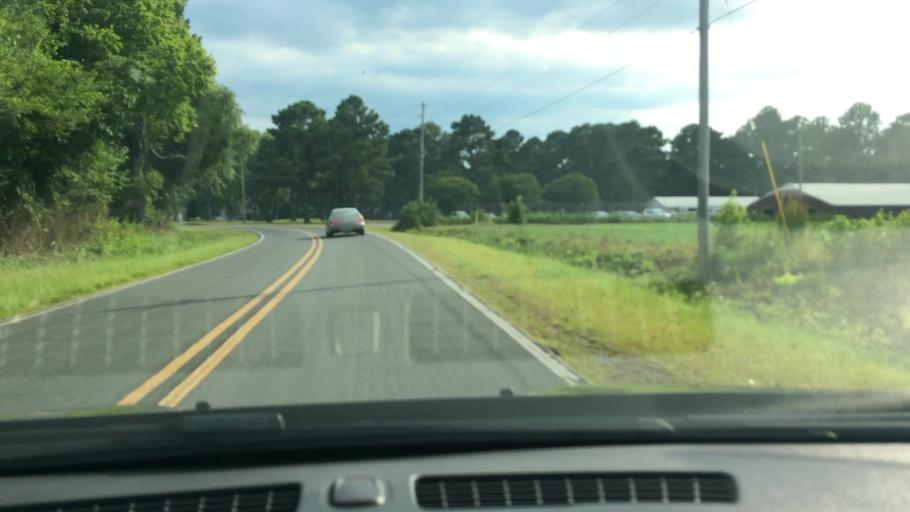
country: US
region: North Carolina
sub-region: Pitt County
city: Ayden
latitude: 35.4648
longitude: -77.3893
